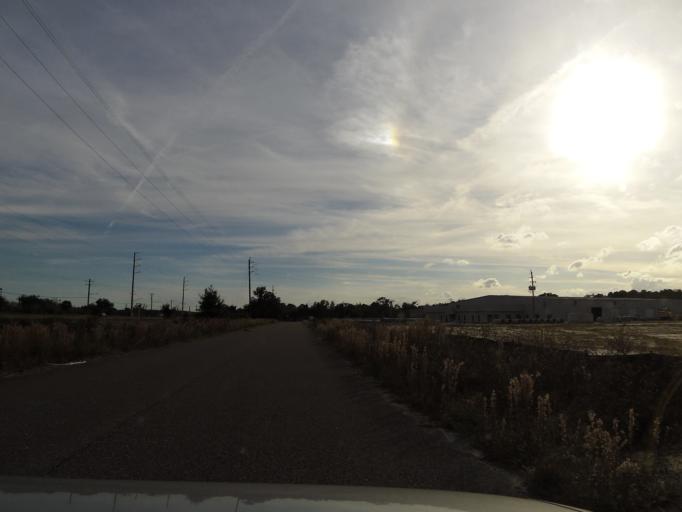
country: US
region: Florida
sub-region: Duval County
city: Jacksonville
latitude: 30.4235
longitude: -81.6479
